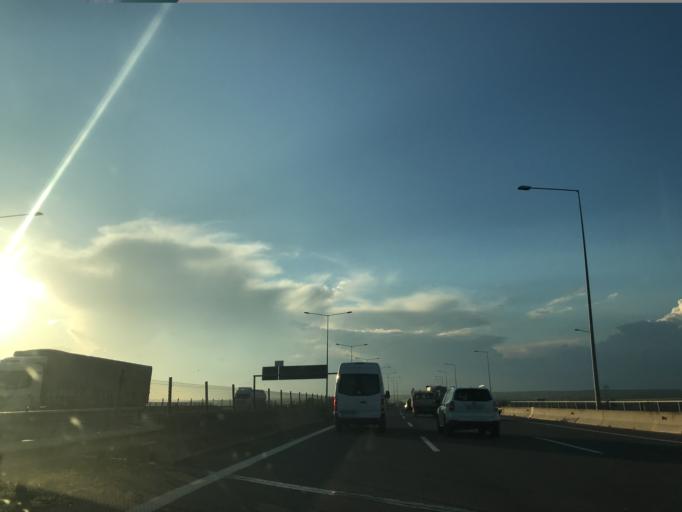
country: TR
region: Adana
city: Yakapinar
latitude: 37.0051
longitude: 35.6962
